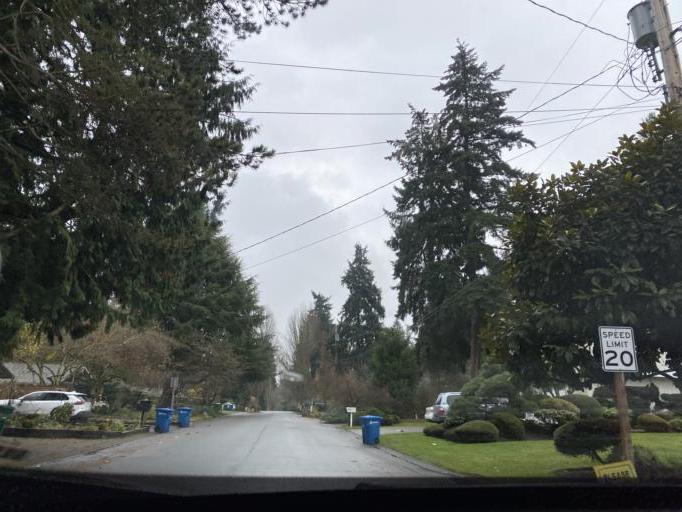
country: US
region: Washington
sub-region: King County
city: Mercer Island
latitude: 47.5461
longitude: -122.2264
